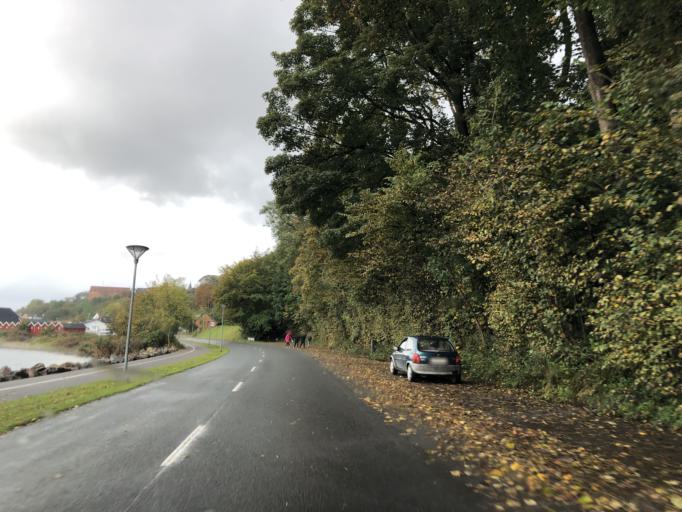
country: DK
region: Central Jutland
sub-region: Lemvig Kommune
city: Lemvig
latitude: 56.5518
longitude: 8.2974
